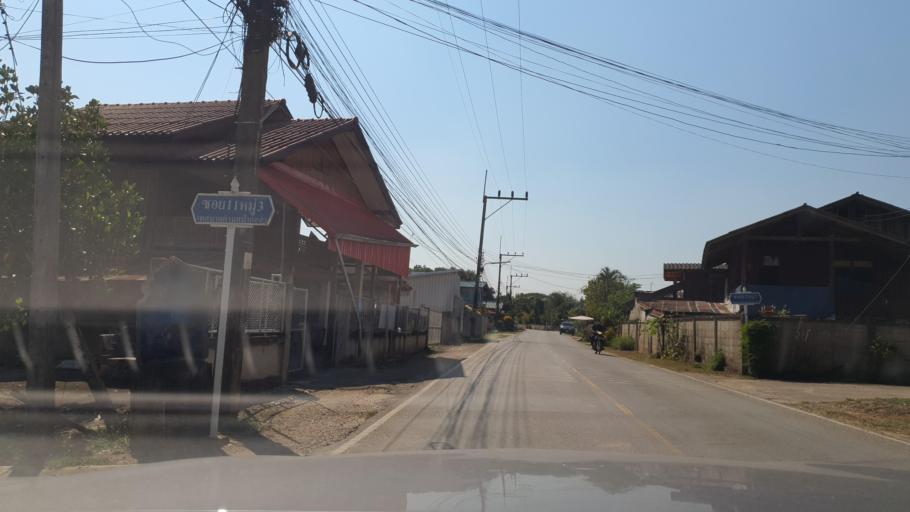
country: TH
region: Chiang Rai
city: Mae Lao
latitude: 19.7643
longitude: 99.7305
